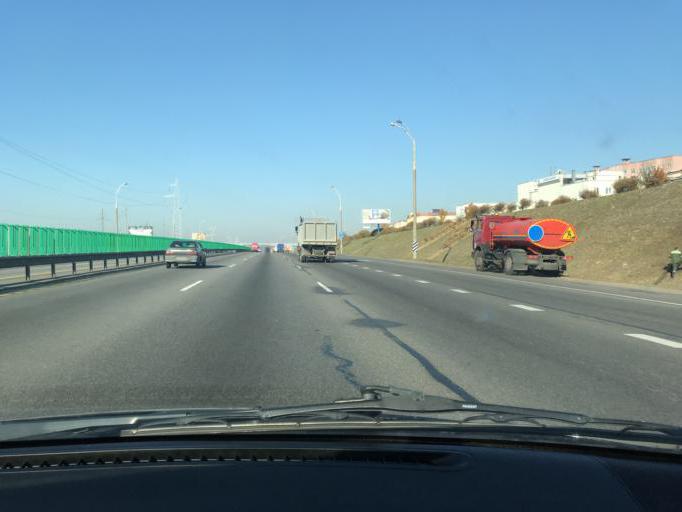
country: BY
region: Minsk
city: Malinovka
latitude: 53.8813
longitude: 27.4172
